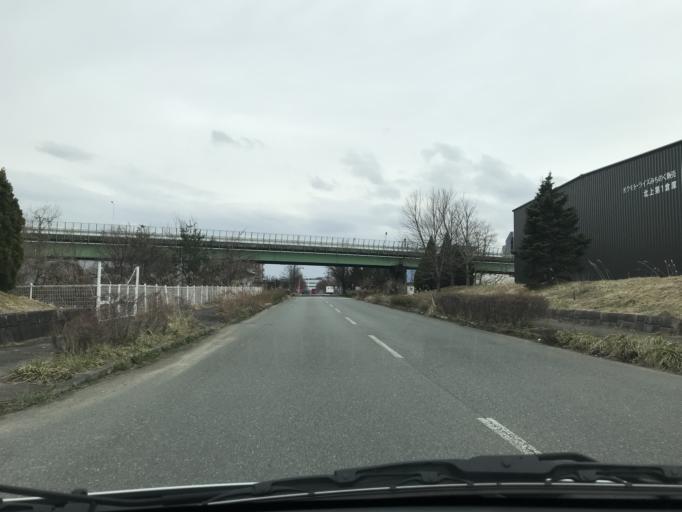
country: JP
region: Iwate
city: Kitakami
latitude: 39.2590
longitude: 141.1081
